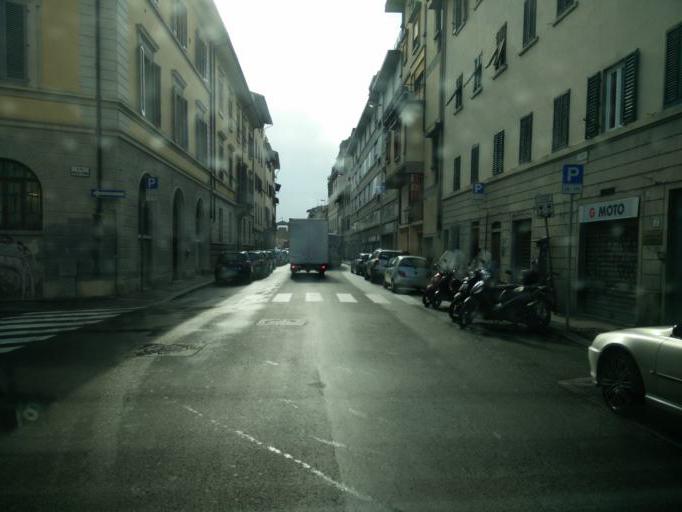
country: IT
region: Tuscany
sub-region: Province of Florence
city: Florence
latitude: 43.7806
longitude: 11.2372
